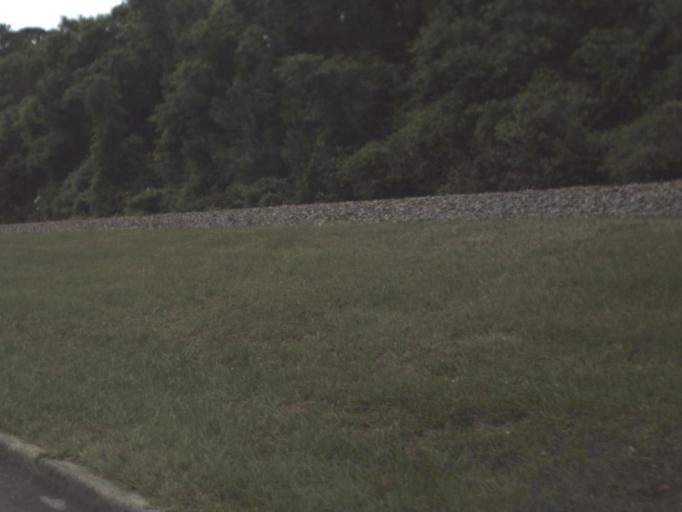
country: US
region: Florida
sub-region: Duval County
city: Jacksonville
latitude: 30.2598
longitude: -81.7013
